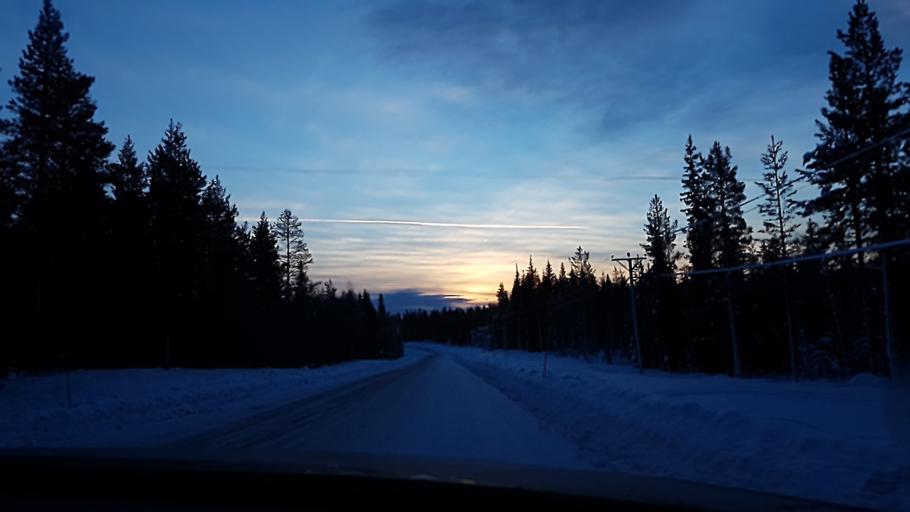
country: SE
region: Norrbotten
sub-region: Jokkmokks Kommun
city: Jokkmokk
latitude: 66.1323
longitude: 20.0015
